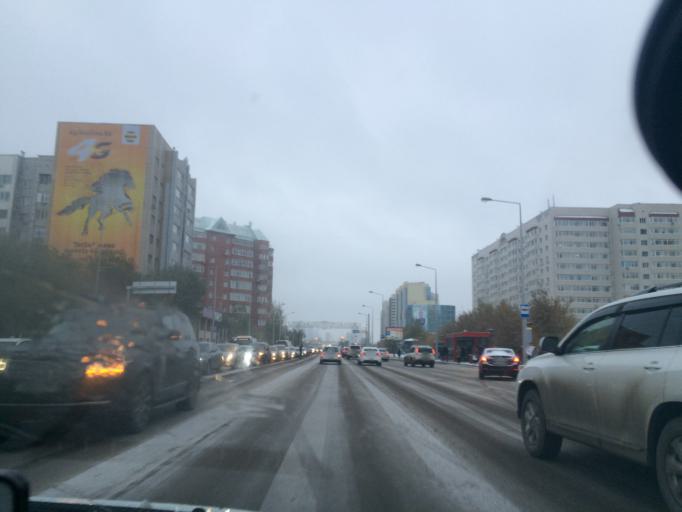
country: KZ
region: Astana Qalasy
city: Astana
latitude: 51.1658
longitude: 71.4089
